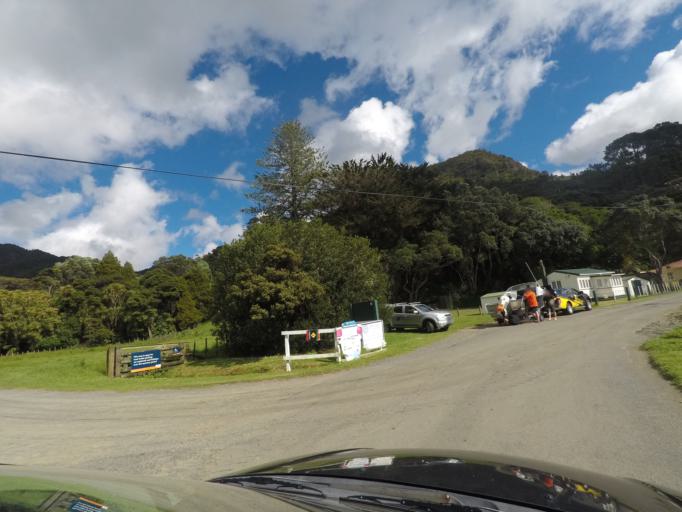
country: NZ
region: Auckland
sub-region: Auckland
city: Titirangi
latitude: -37.0161
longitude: 174.5582
